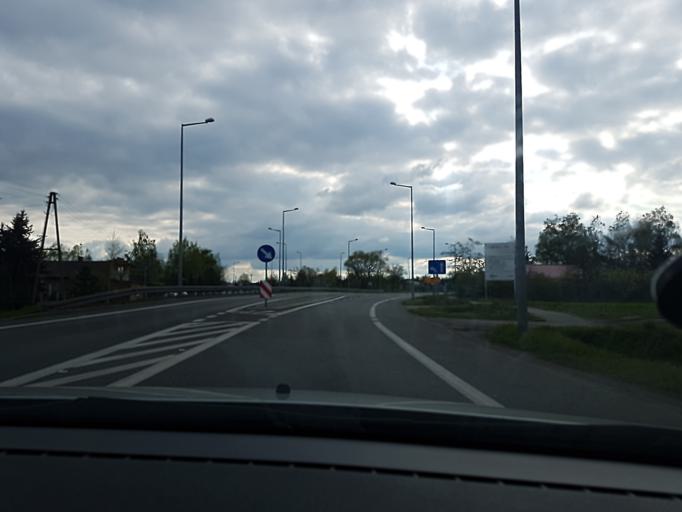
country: PL
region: Lodz Voivodeship
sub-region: powiat Lowicki
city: Lowicz
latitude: 52.1172
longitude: 19.9767
